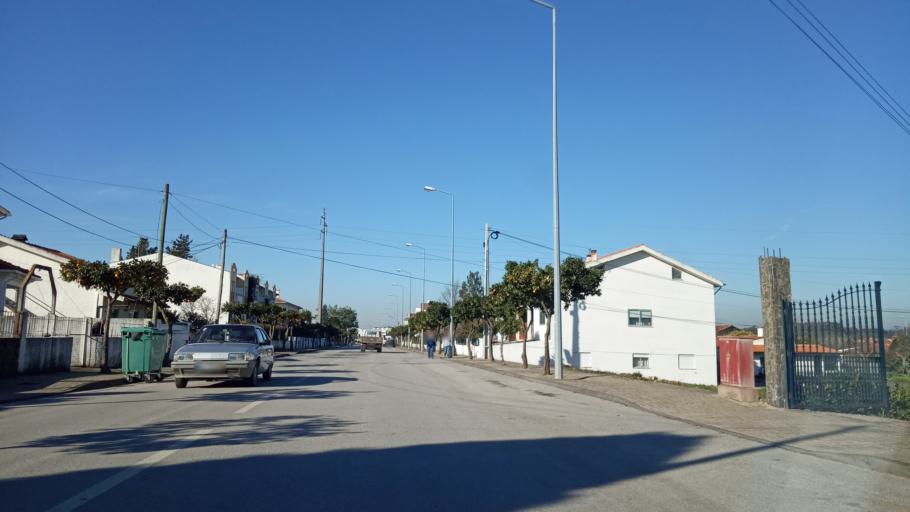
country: PT
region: Aveiro
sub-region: Anadia
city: Anadia
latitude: 40.4383
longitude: -8.4318
